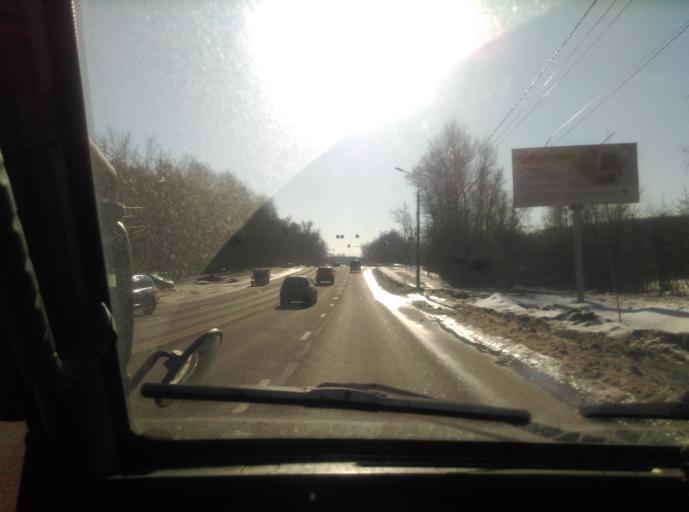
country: RU
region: Moskovskaya
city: Domodedovo
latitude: 55.4178
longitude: 37.7783
